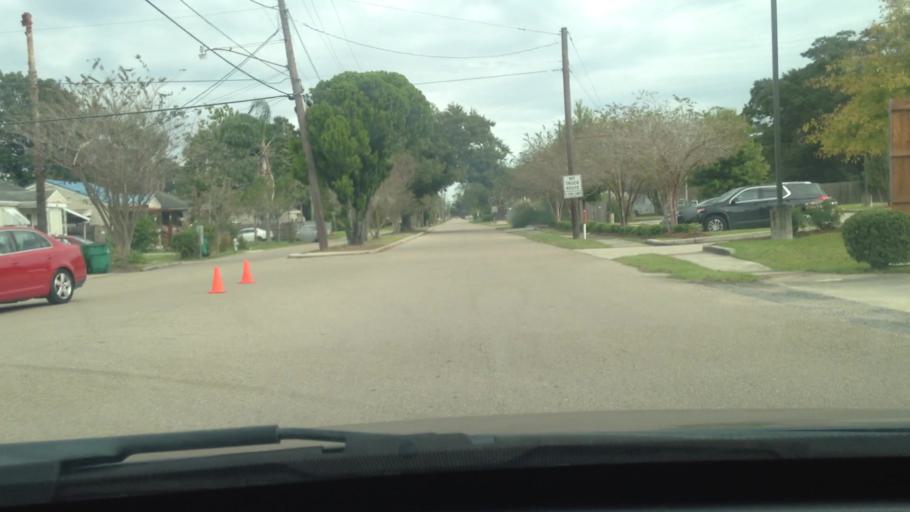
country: US
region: Louisiana
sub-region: Jefferson Parish
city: River Ridge
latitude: 29.9790
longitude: -90.2201
